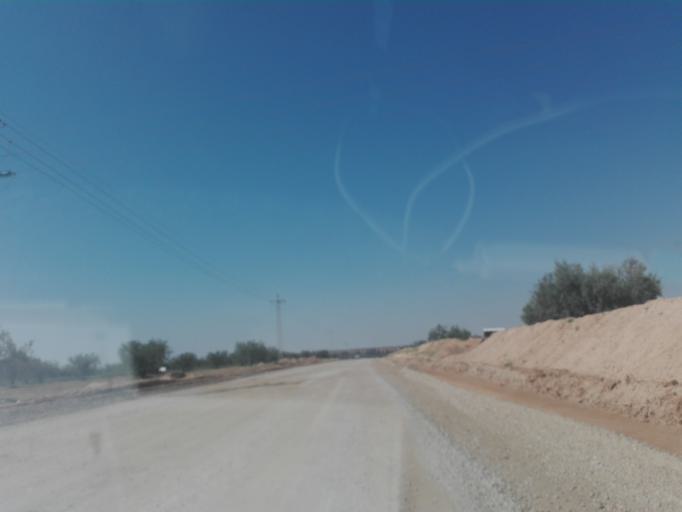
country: TN
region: Safaqis
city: Sfax
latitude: 34.7000
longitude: 10.4830
